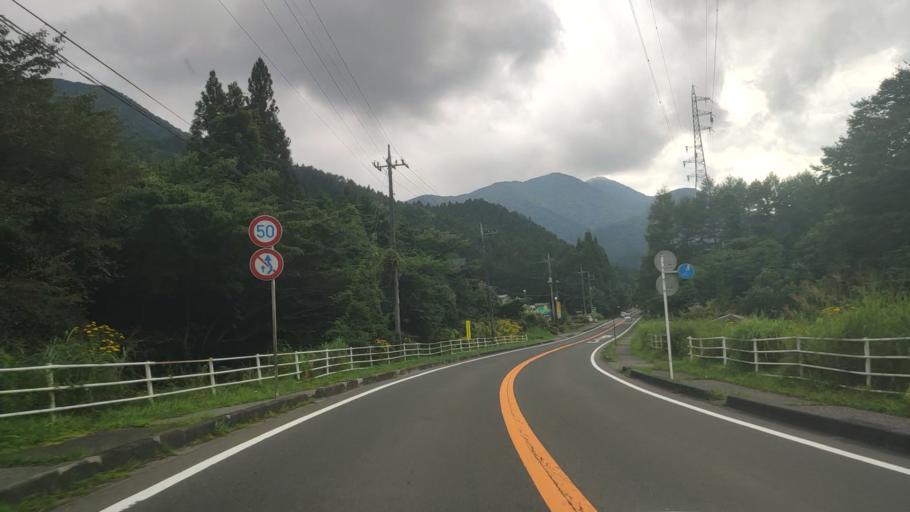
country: JP
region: Tochigi
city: Nikko
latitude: 36.7281
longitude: 139.5482
